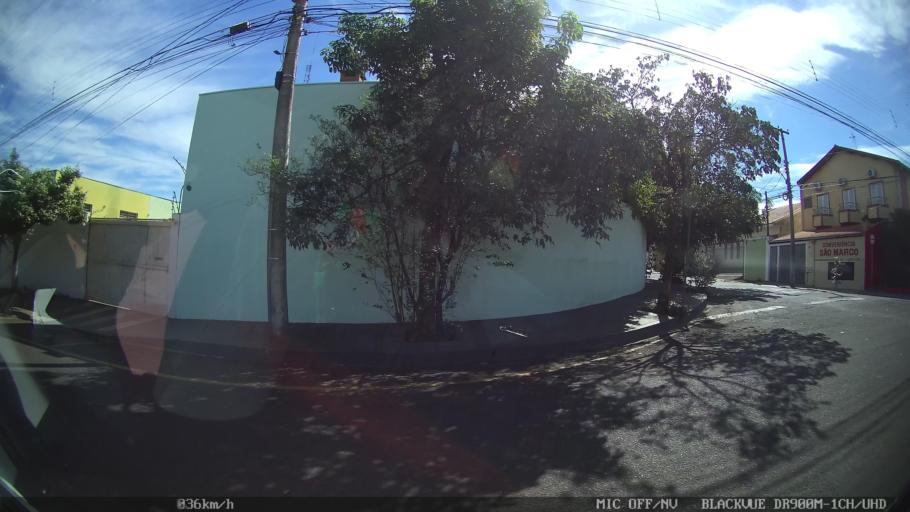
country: BR
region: Sao Paulo
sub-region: Sao Jose Do Rio Preto
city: Sao Jose do Rio Preto
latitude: -20.8411
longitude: -49.3605
